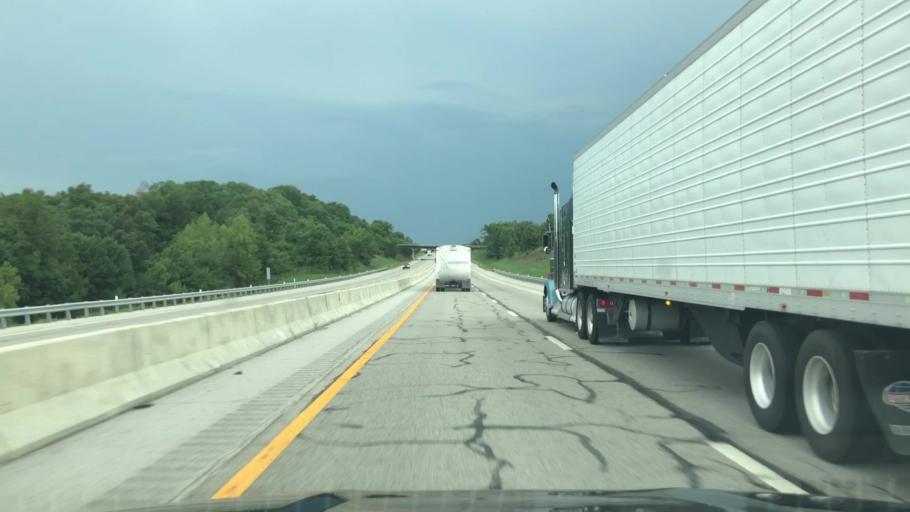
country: US
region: Oklahoma
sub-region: Rogers County
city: Bushyhead
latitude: 36.4196
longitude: -95.3985
